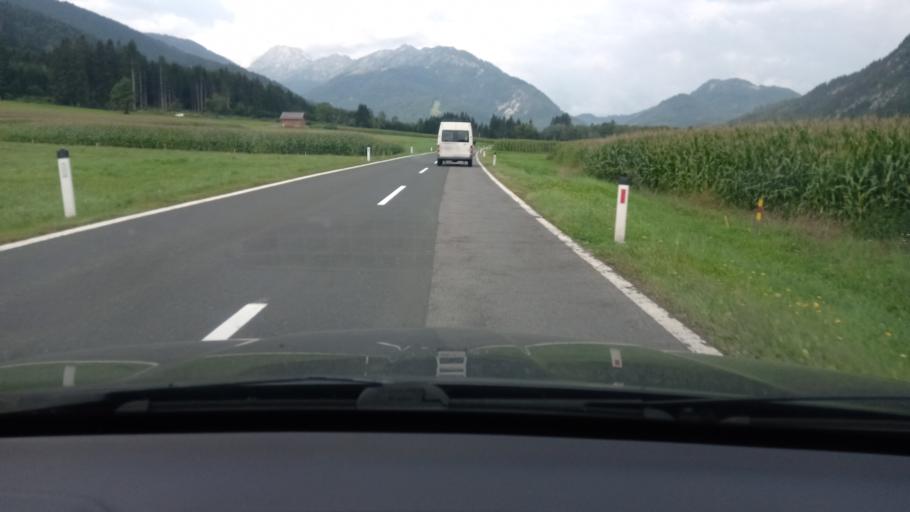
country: AT
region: Carinthia
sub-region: Politischer Bezirk Hermagor
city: Hermagor
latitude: 46.6693
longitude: 13.2908
